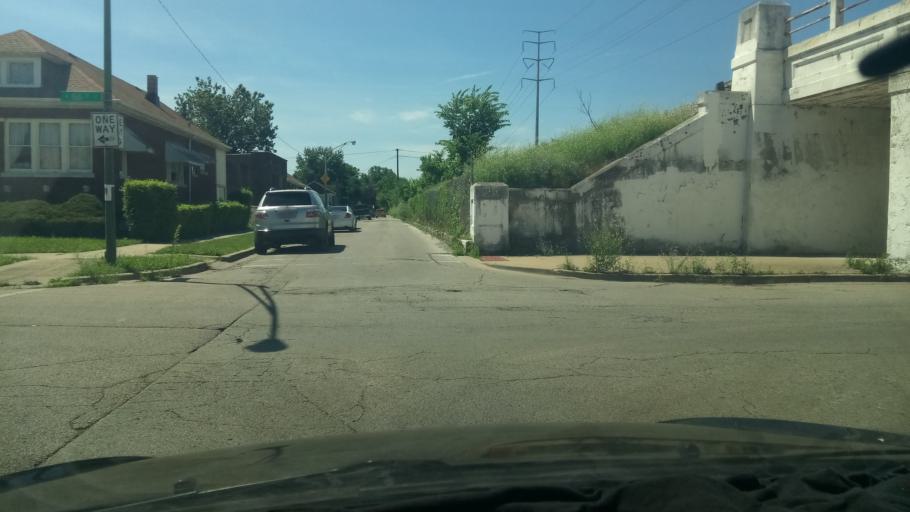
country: US
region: Illinois
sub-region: Cook County
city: Hometown
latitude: 41.7737
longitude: -87.7125
